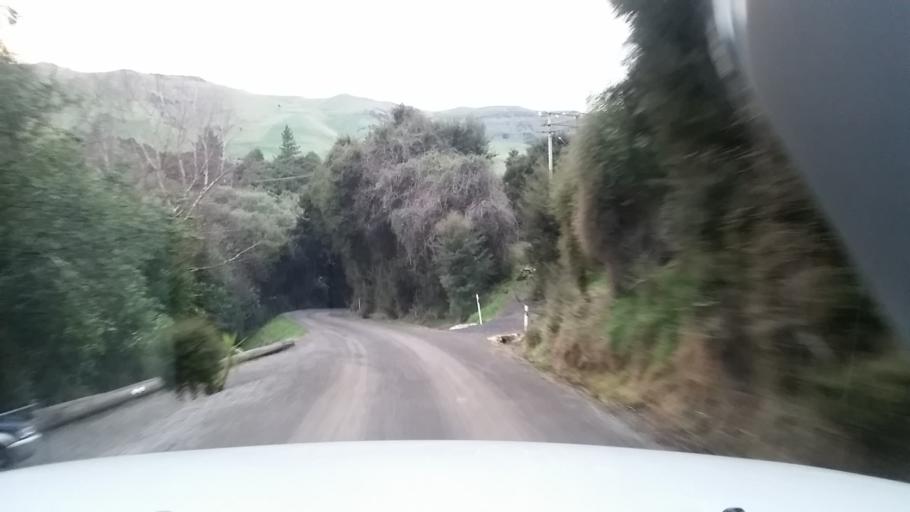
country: NZ
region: Canterbury
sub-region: Christchurch City
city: Christchurch
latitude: -43.7347
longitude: 172.7842
